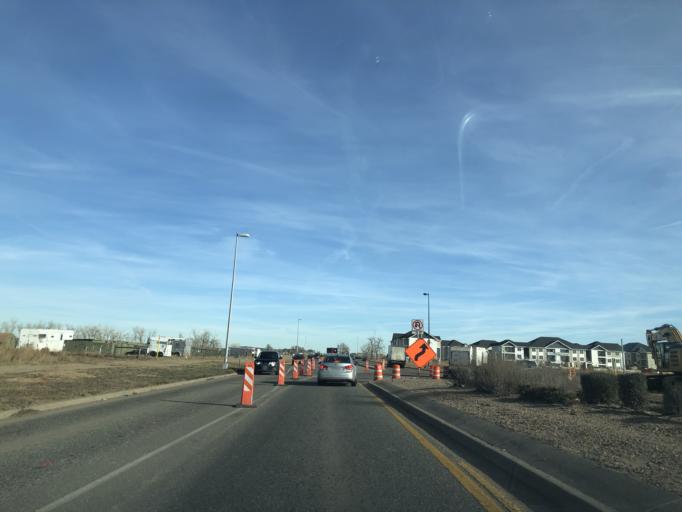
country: US
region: Colorado
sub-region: Adams County
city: Aurora
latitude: 39.7983
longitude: -104.7821
